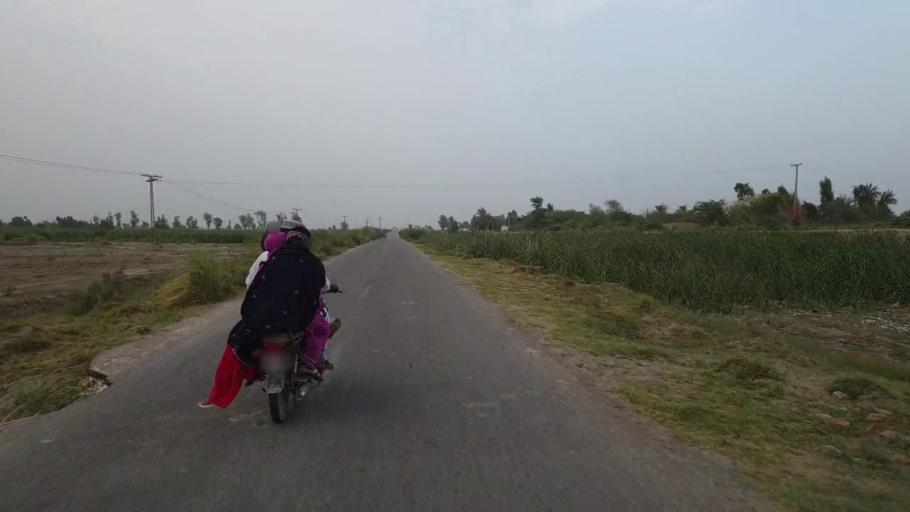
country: PK
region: Sindh
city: Daur
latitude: 26.4542
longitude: 68.2923
